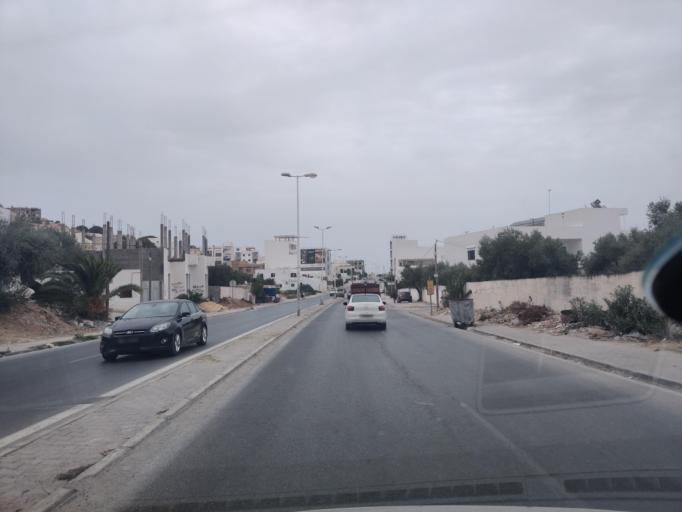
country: TN
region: Nabul
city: Al Hammamat
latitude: 36.4090
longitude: 10.6255
